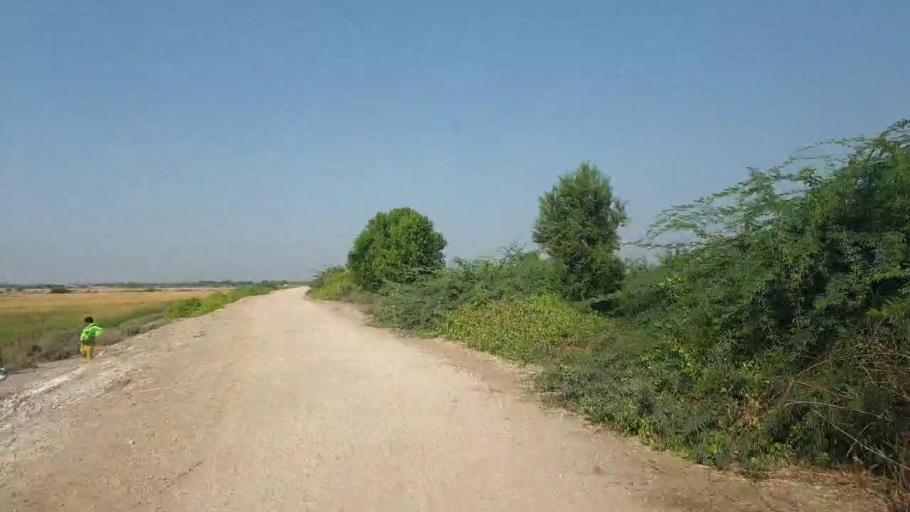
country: PK
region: Sindh
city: Badin
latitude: 24.5206
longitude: 68.7740
